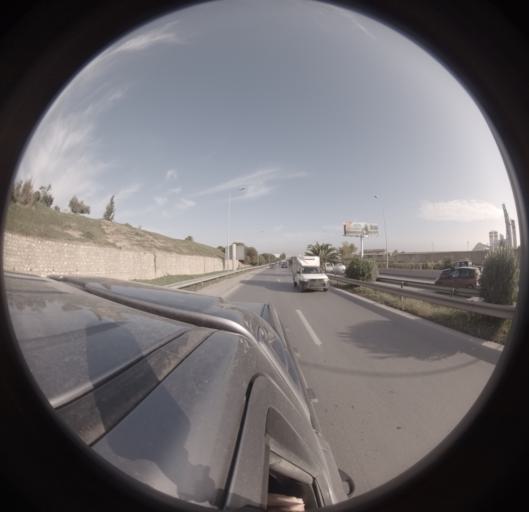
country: TN
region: Bin 'Arus
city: Ben Arous
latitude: 36.7777
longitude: 10.1970
